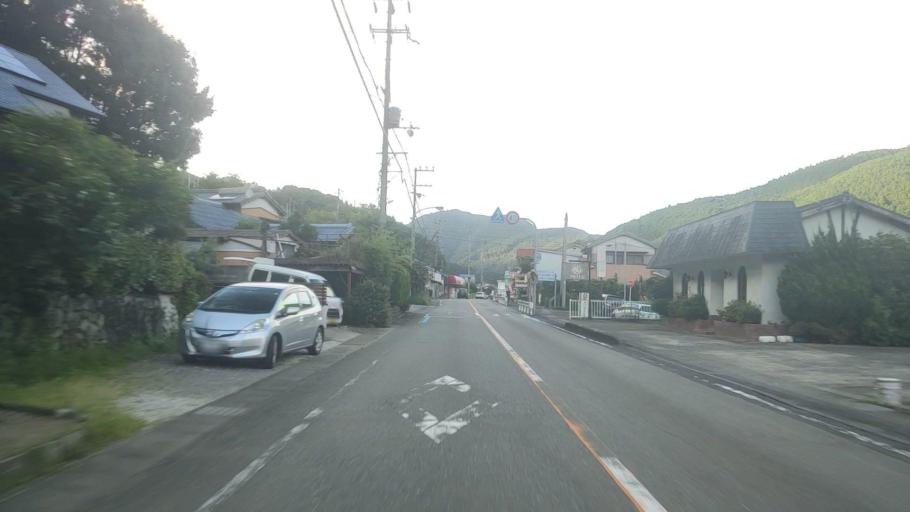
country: JP
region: Wakayama
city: Tanabe
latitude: 33.7911
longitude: 135.5163
